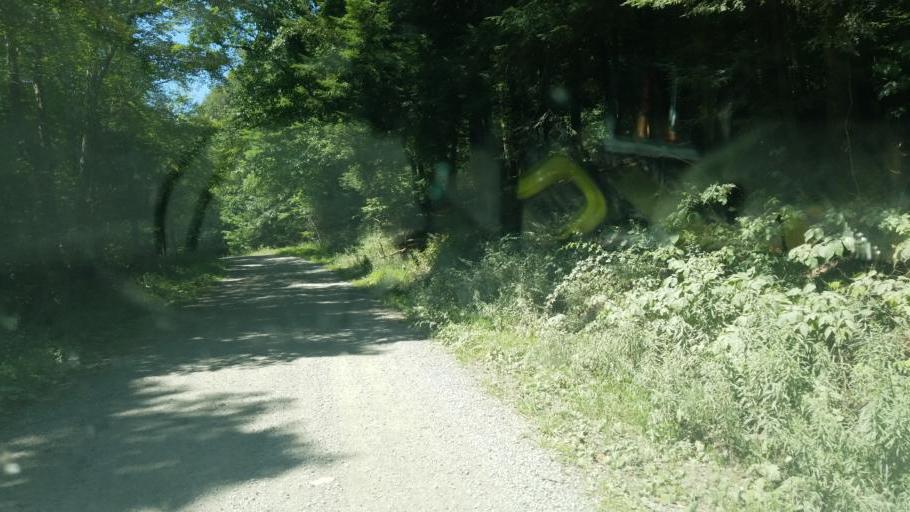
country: US
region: Pennsylvania
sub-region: Clarion County
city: Marianne
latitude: 41.1769
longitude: -79.4477
